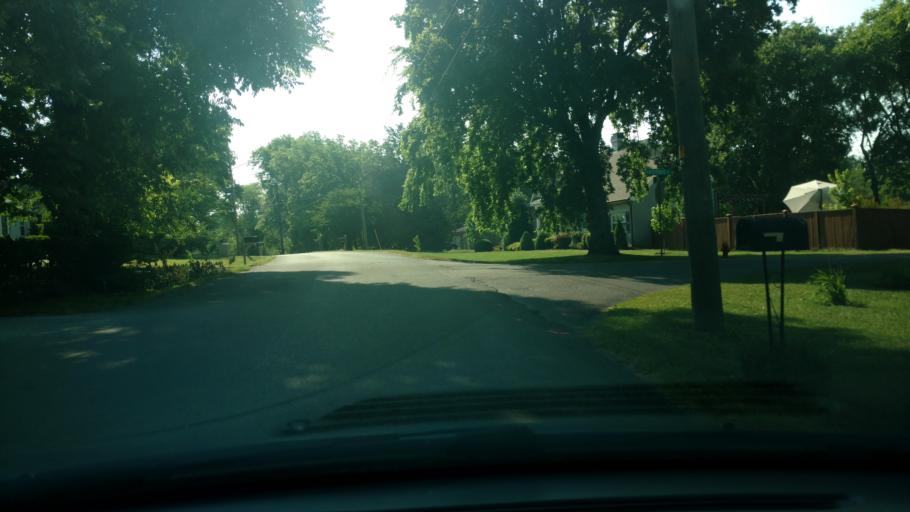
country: US
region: Tennessee
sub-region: Davidson County
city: Nashville
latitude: 36.2243
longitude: -86.7214
